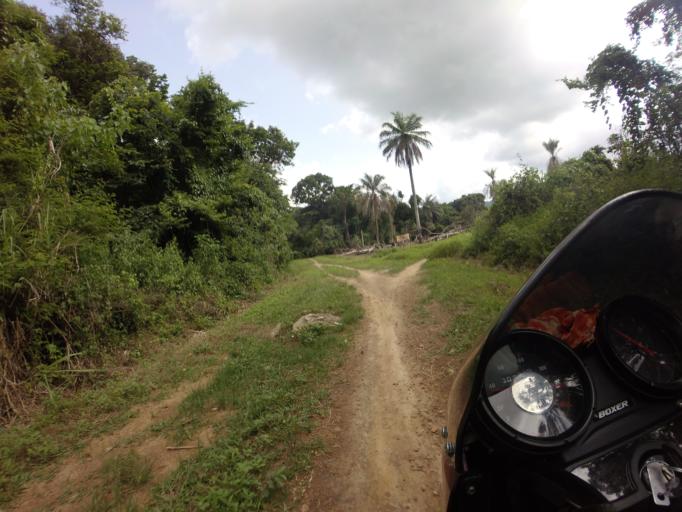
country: SL
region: Eastern Province
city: Tombu
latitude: 8.5470
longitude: -10.7283
